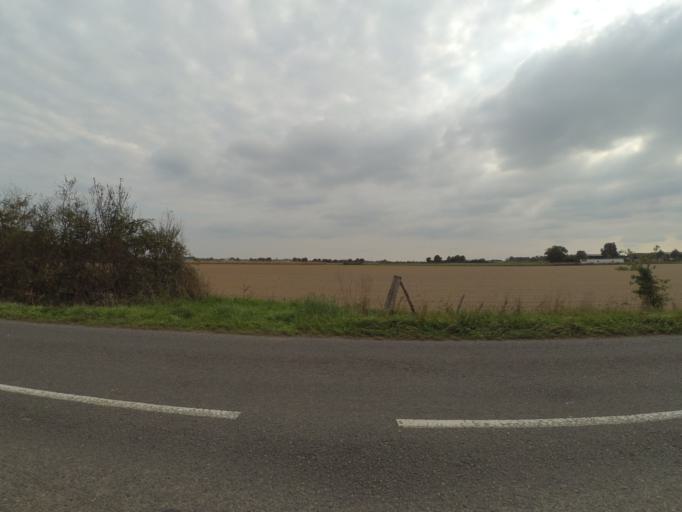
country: FR
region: Pays de la Loire
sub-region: Departement de la Loire-Atlantique
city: Vieillevigne
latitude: 46.9880
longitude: -1.3942
